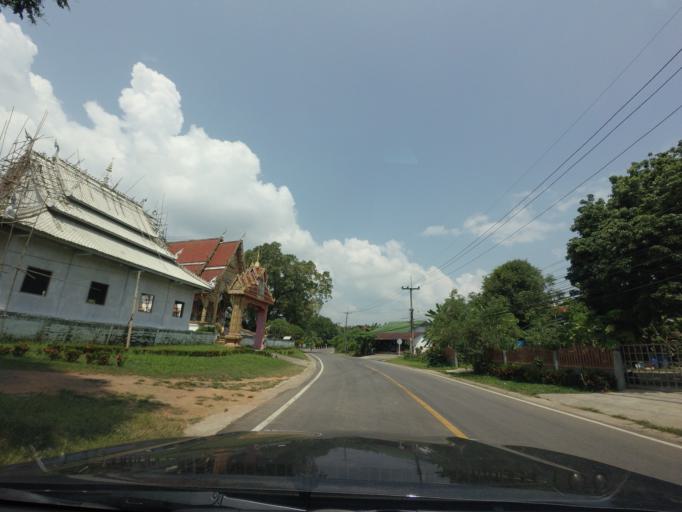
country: TH
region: Nan
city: Santi Suk
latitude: 18.9516
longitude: 100.9229
